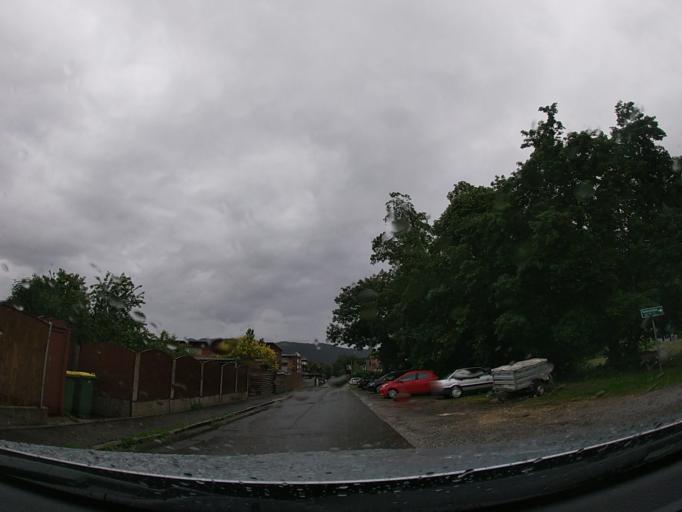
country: AT
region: Styria
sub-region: Politischer Bezirk Leoben
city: Trofaiach
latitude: 47.4215
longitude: 14.9925
